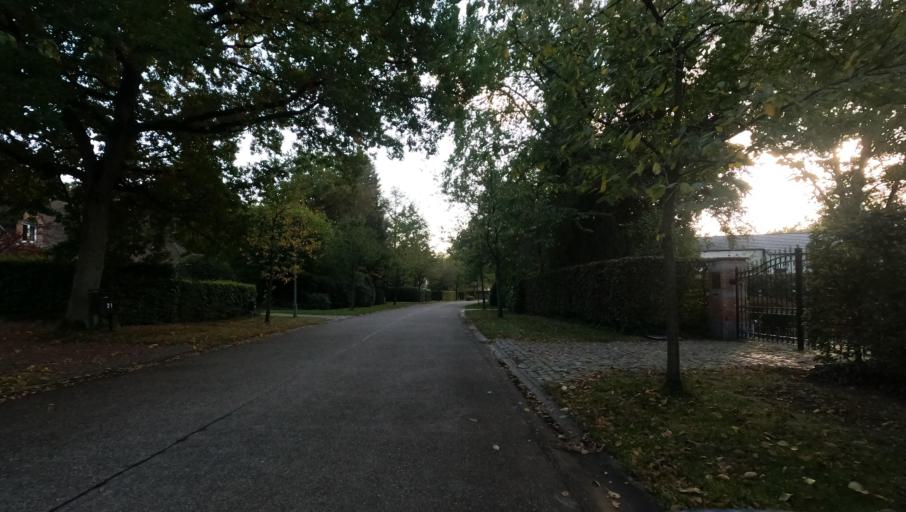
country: BE
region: Flanders
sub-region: Provincie Antwerpen
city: Schilde
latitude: 51.2423
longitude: 4.5683
